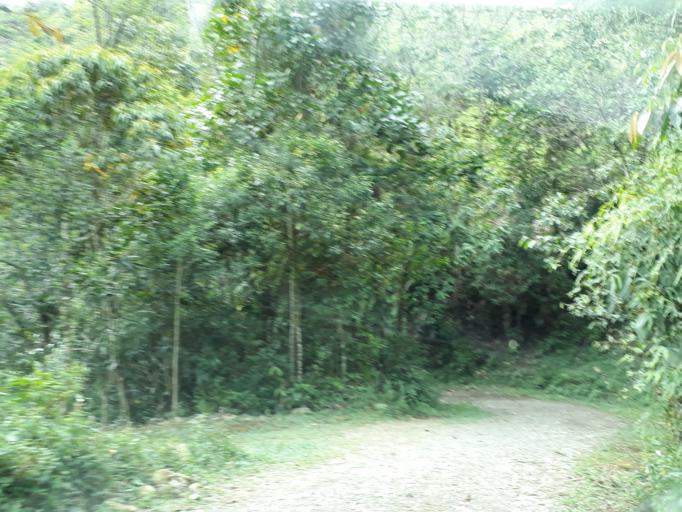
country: CO
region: Boyaca
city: Quipama
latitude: 5.3932
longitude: -74.1217
